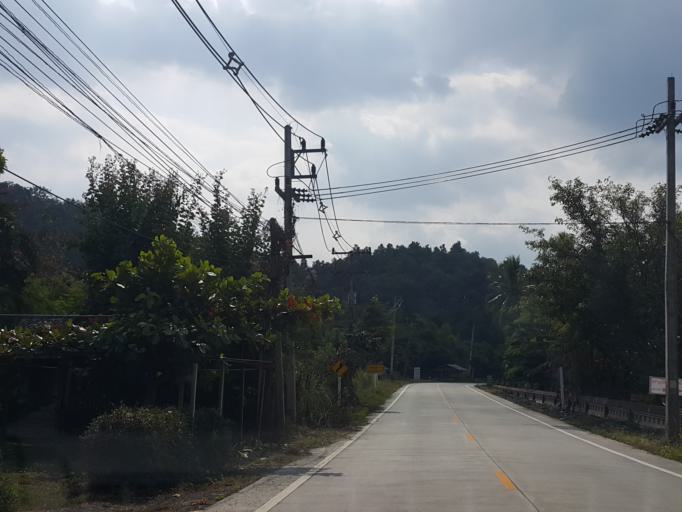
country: TH
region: Chiang Mai
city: Mae On
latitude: 18.8104
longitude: 99.2372
